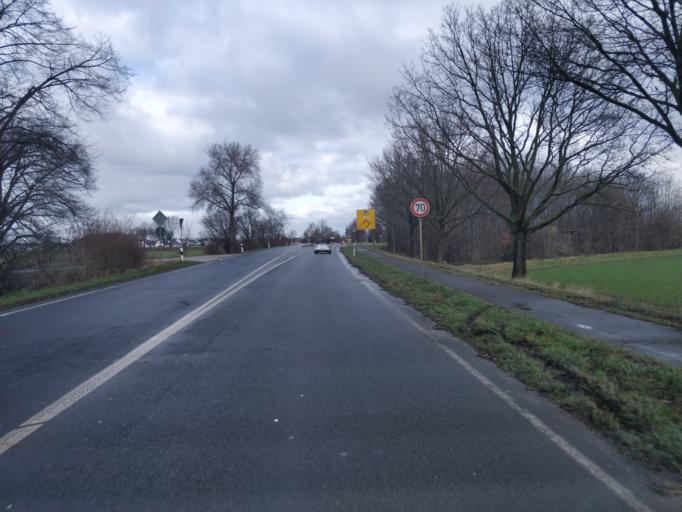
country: DE
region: North Rhine-Westphalia
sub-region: Regierungsbezirk Koln
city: Euskirchen
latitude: 50.6408
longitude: 6.8413
